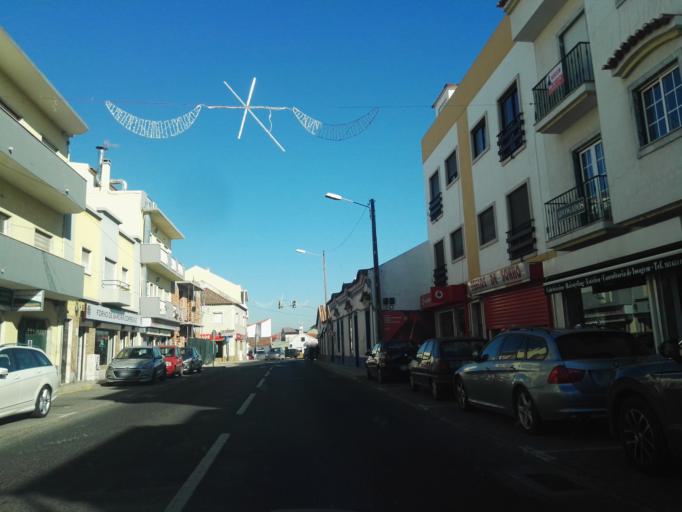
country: PT
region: Santarem
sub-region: Benavente
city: Samora Correia
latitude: 38.9363
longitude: -8.8710
